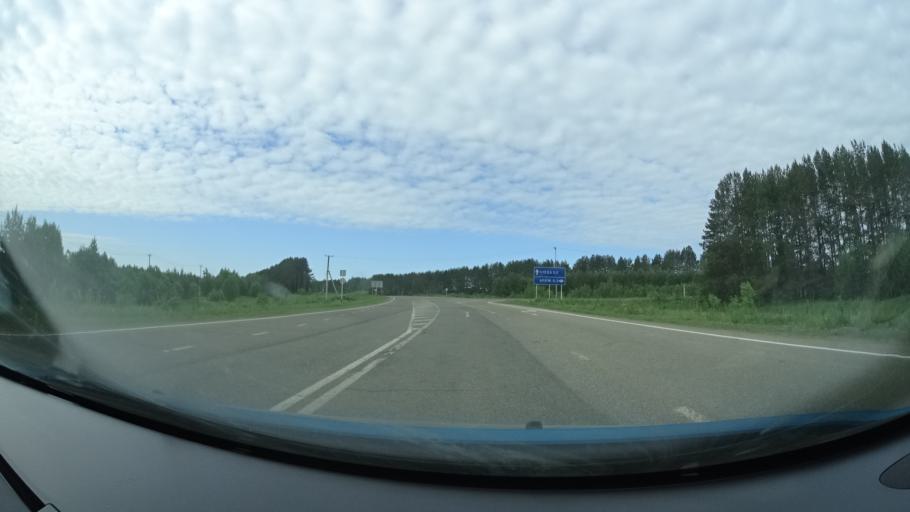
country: RU
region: Perm
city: Kuyeda
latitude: 56.4941
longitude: 55.6010
